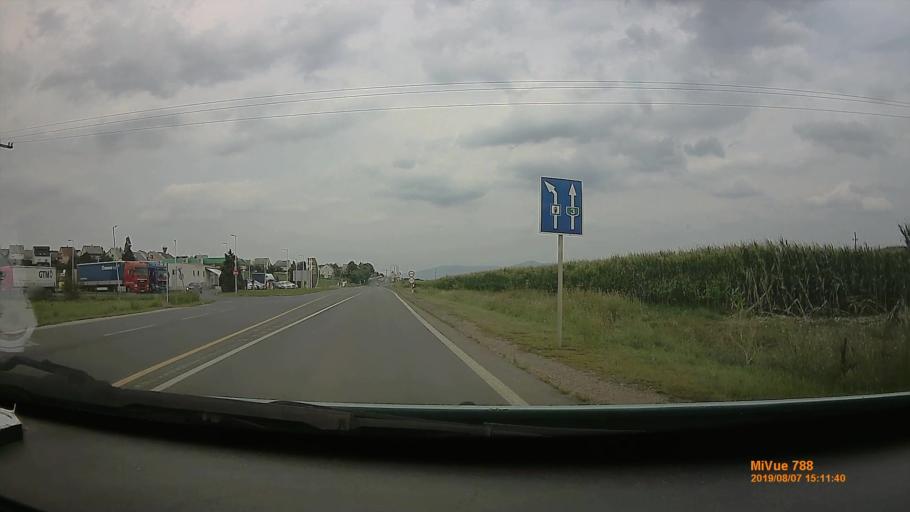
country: HU
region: Borsod-Abauj-Zemplen
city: Encs
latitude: 48.3332
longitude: 21.1023
